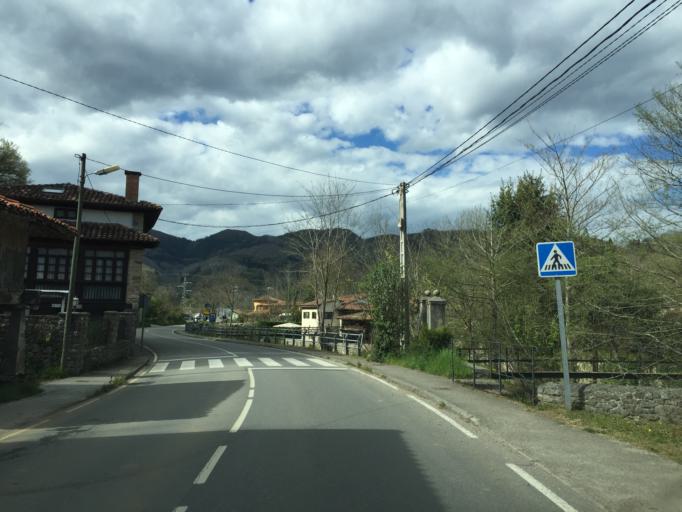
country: ES
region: Asturias
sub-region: Province of Asturias
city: Cangas de Onis
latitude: 43.3443
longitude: -5.0839
